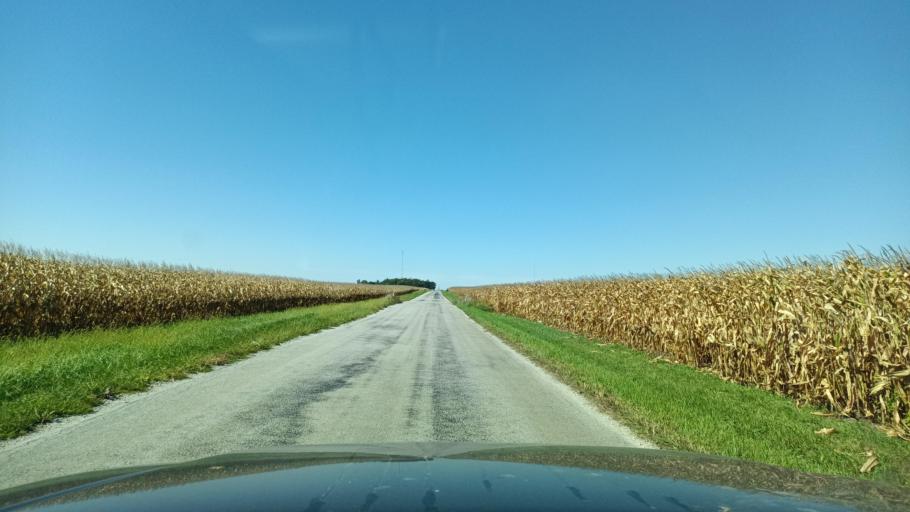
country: US
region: Illinois
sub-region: Champaign County
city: Mahomet
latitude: 40.0987
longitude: -88.3842
